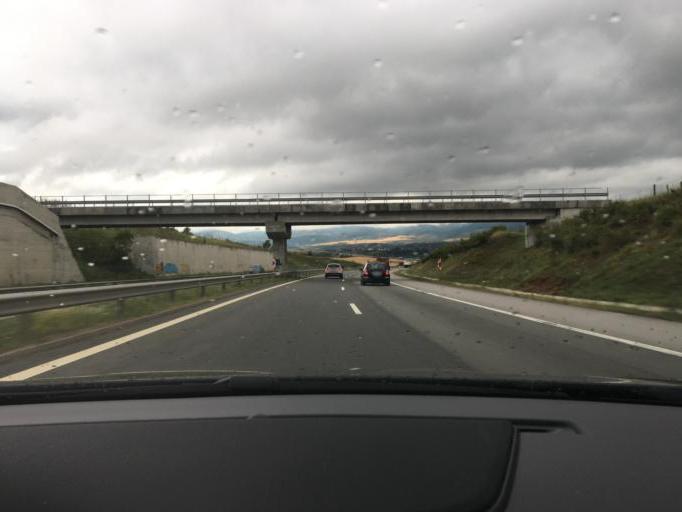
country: BG
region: Pernik
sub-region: Obshtina Pernik
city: Pernik
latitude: 42.6135
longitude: 23.1381
